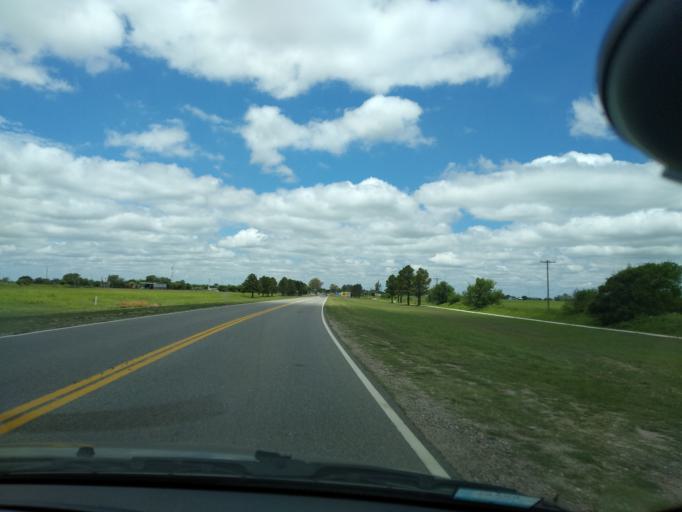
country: AR
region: Cordoba
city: Toledo
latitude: -31.6483
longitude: -64.1010
